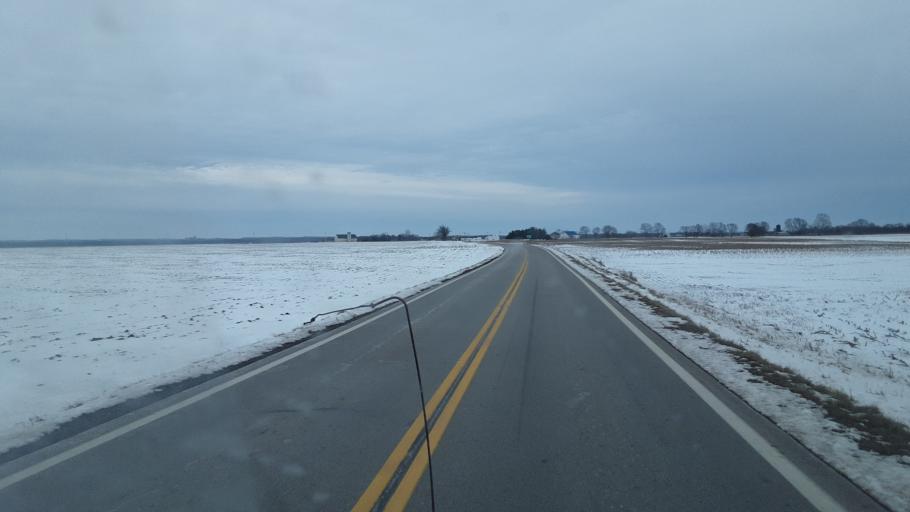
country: US
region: Ohio
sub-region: Pickaway County
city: Circleville
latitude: 39.6162
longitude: -83.0143
